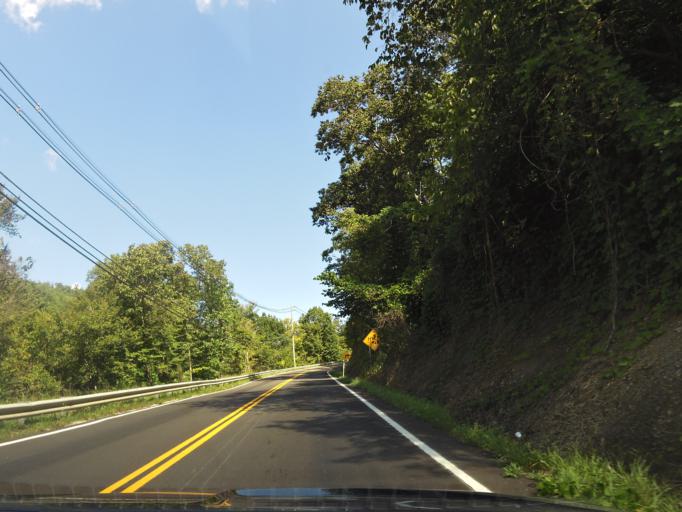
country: US
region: Kentucky
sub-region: Clay County
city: Manchester
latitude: 37.0961
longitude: -83.6681
